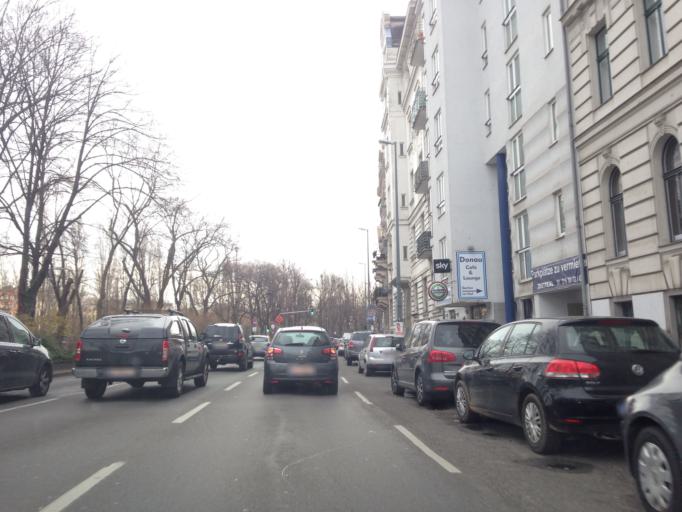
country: AT
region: Vienna
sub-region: Wien Stadt
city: Vienna
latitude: 48.2262
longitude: 16.3657
